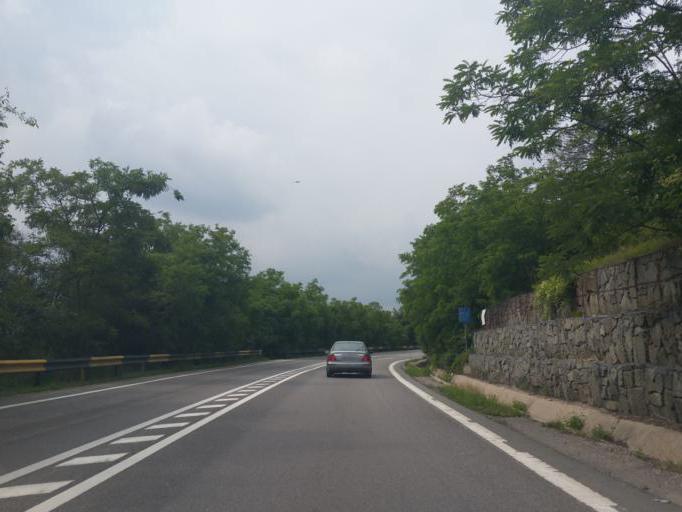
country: RO
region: Salaj
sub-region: Comuna Treznea
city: Treznea
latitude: 47.1259
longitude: 23.1296
